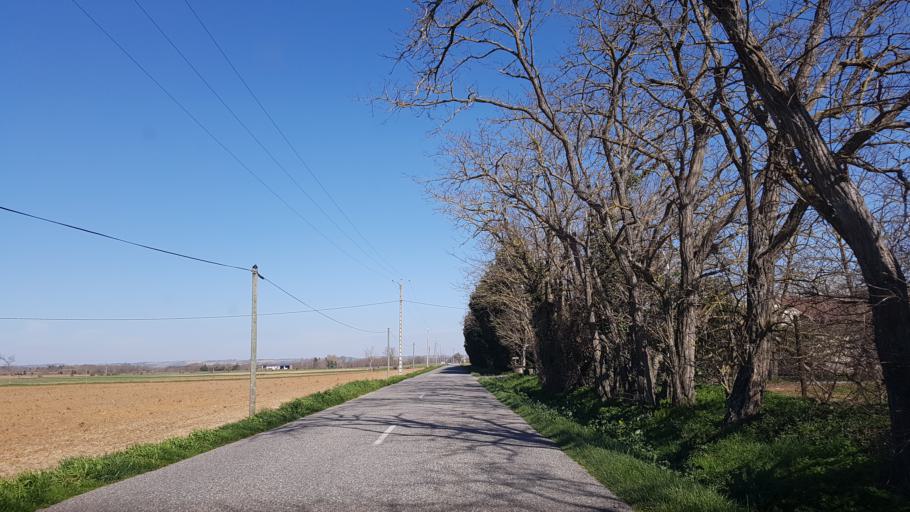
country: FR
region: Languedoc-Roussillon
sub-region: Departement de l'Aude
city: Belpech
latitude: 43.1769
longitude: 1.7108
